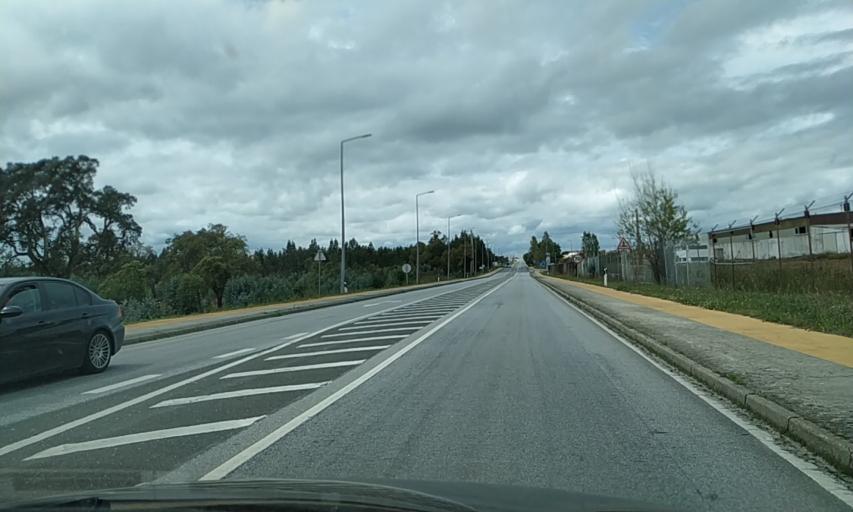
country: PT
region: Evora
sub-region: Vendas Novas
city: Vendas Novas
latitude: 38.6685
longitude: -8.4374
